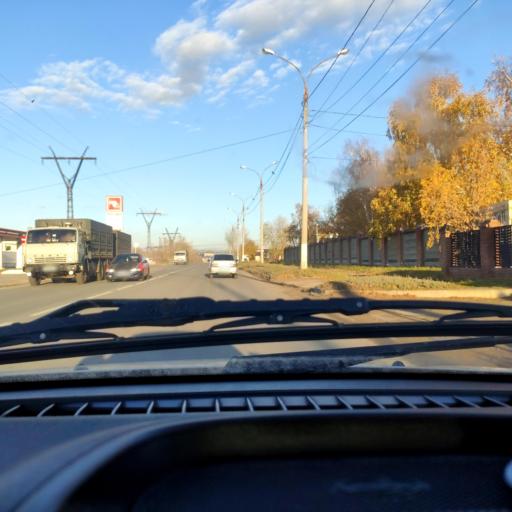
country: RU
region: Samara
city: Zhigulevsk
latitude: 53.4799
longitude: 49.4979
